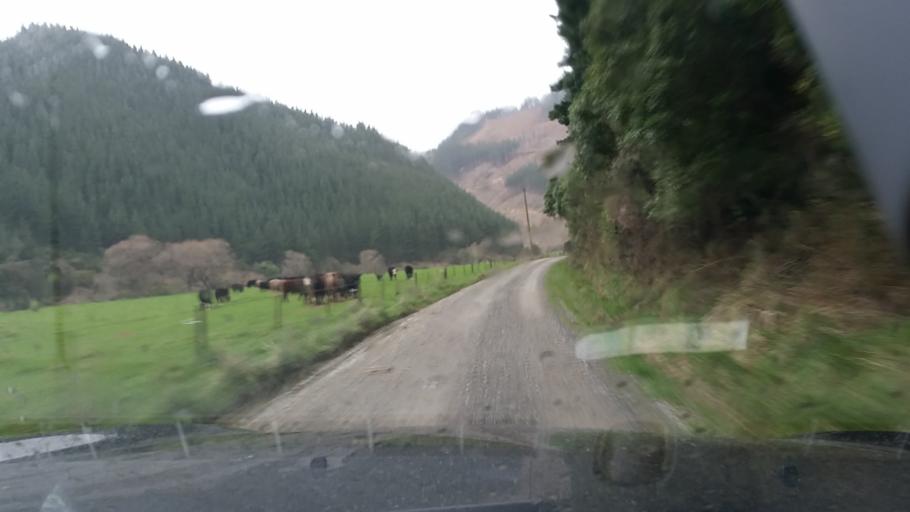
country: NZ
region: Marlborough
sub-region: Marlborough District
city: Blenheim
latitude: -41.3950
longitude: 173.8507
